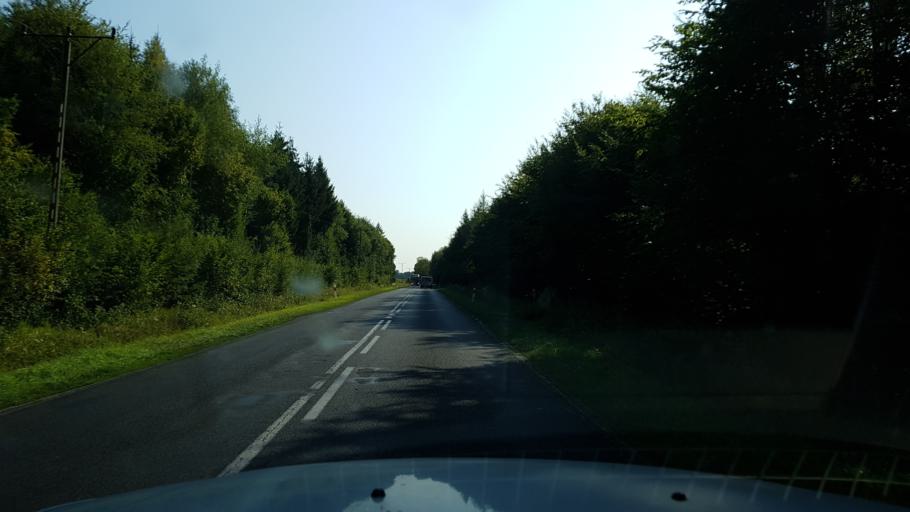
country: PL
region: West Pomeranian Voivodeship
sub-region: Powiat lobeski
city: Resko
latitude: 53.7786
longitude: 15.3525
